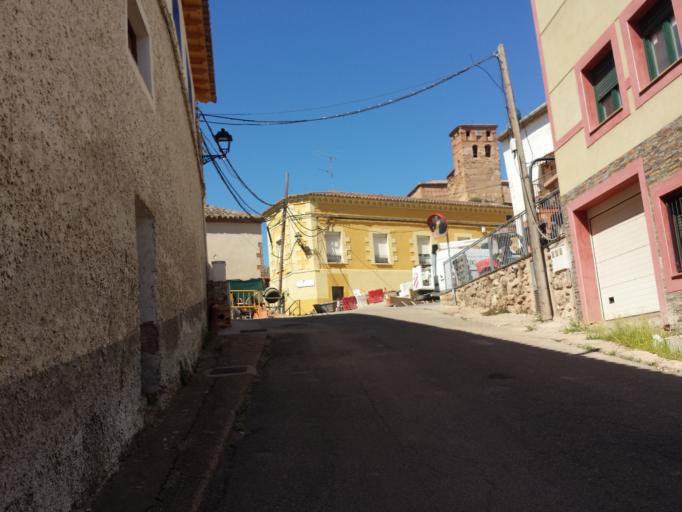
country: ES
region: Aragon
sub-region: Provincia de Zaragoza
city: Nuevalos
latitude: 41.2118
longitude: -1.7910
